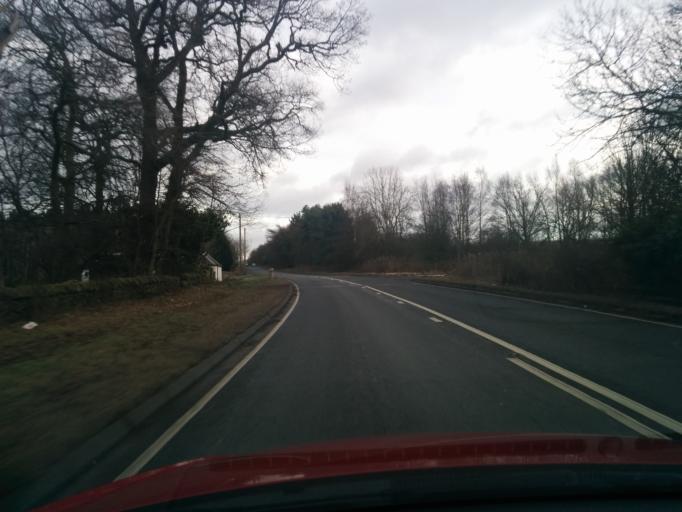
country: GB
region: Scotland
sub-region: West Lothian
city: Broxburn
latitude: 55.9809
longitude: -3.4995
